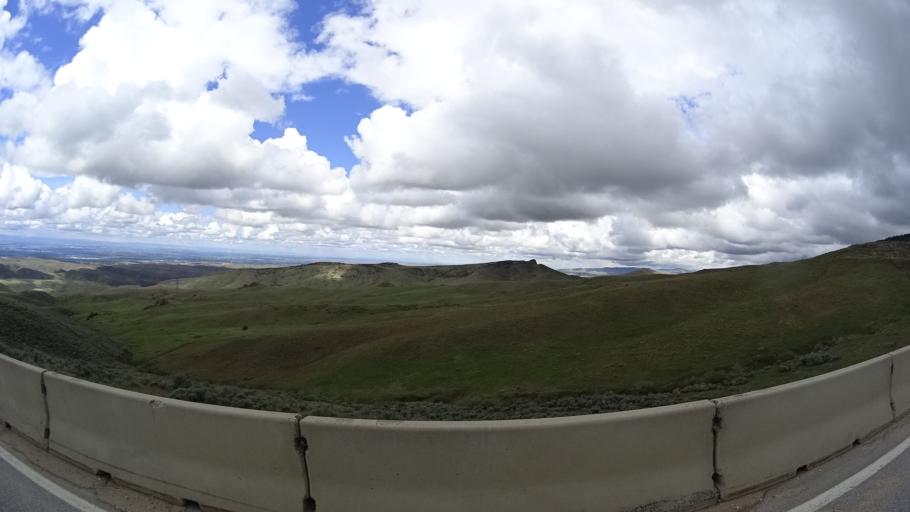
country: US
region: Idaho
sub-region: Ada County
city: Boise
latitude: 43.7083
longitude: -116.1651
